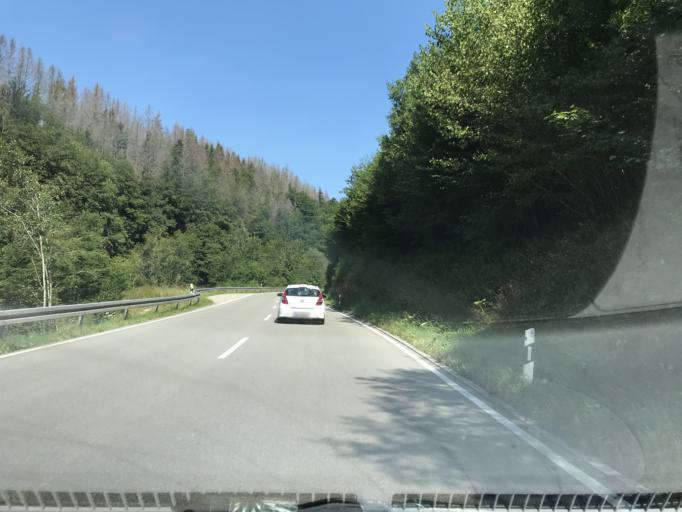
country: DE
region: Baden-Wuerttemberg
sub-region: Freiburg Region
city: Wembach
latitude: 47.7509
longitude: 7.8866
